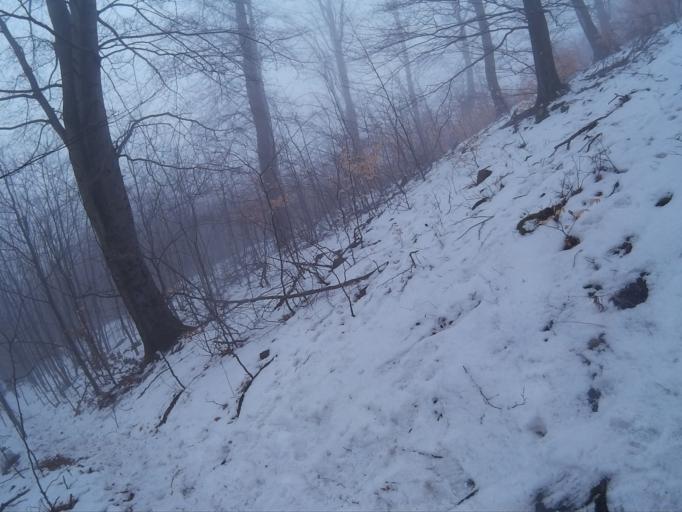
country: HU
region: Heves
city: Domoszlo
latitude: 47.8797
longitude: 20.0773
